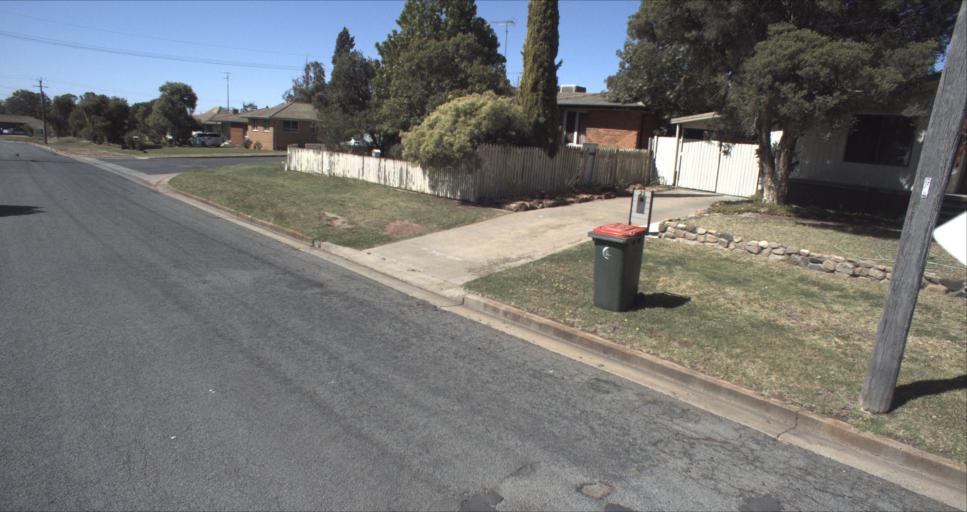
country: AU
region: New South Wales
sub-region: Leeton
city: Leeton
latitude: -34.5495
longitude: 146.3744
